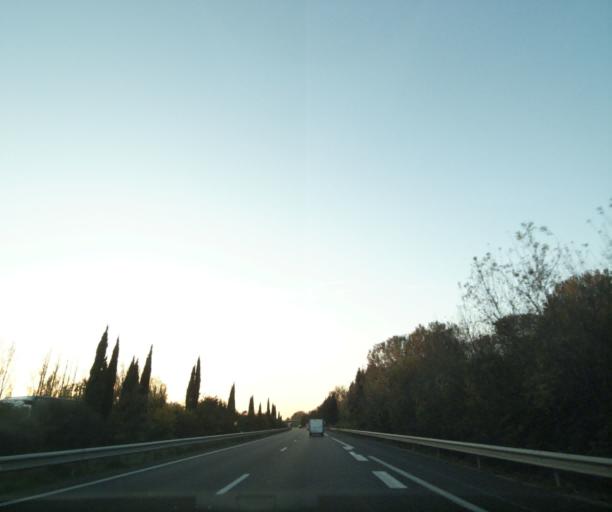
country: FR
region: Provence-Alpes-Cote d'Azur
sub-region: Departement des Bouches-du-Rhone
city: Saint-Martin-de-Crau
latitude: 43.6382
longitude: 4.8510
